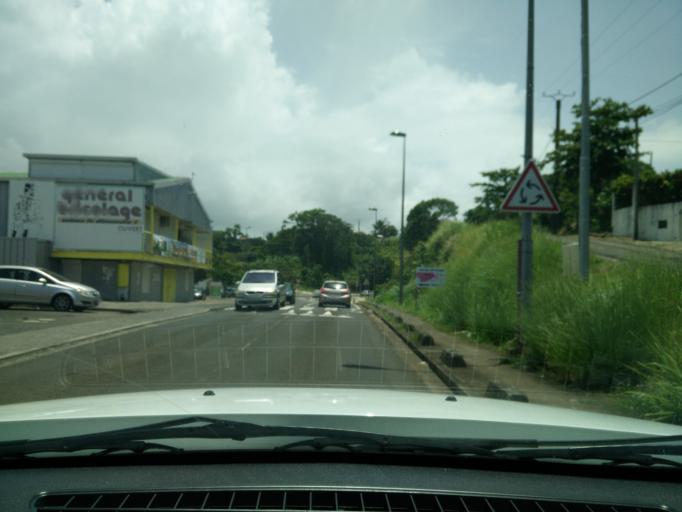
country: GP
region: Guadeloupe
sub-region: Guadeloupe
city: Petit-Bourg
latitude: 16.1334
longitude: -61.5793
